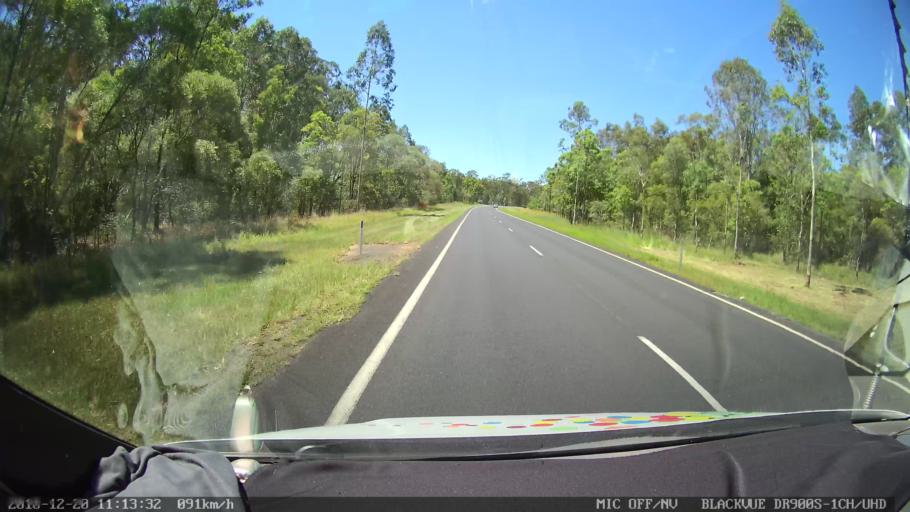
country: AU
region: New South Wales
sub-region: Richmond Valley
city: Casino
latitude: -28.9890
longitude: 153.0110
